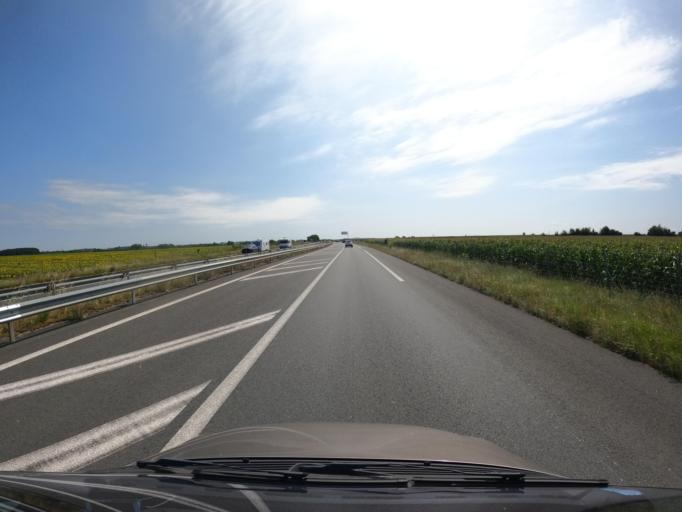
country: FR
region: Poitou-Charentes
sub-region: Departement des Deux-Sevres
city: Mauze-sur-le-Mignon
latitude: 46.1965
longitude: -0.6969
